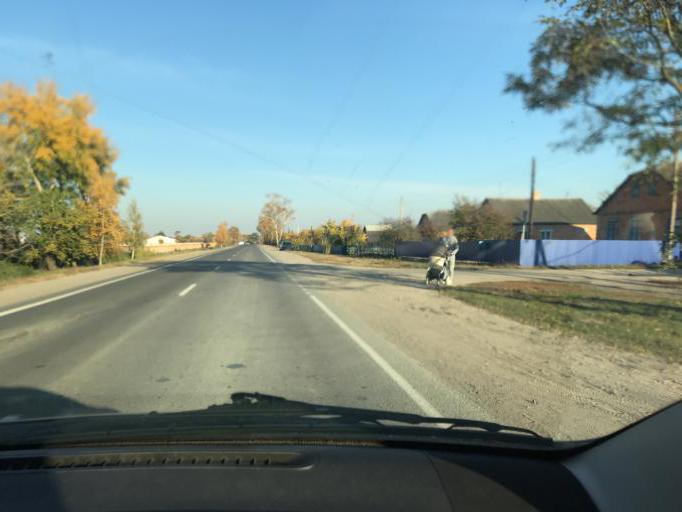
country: BY
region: Brest
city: Stolin
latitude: 51.8463
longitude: 26.7743
